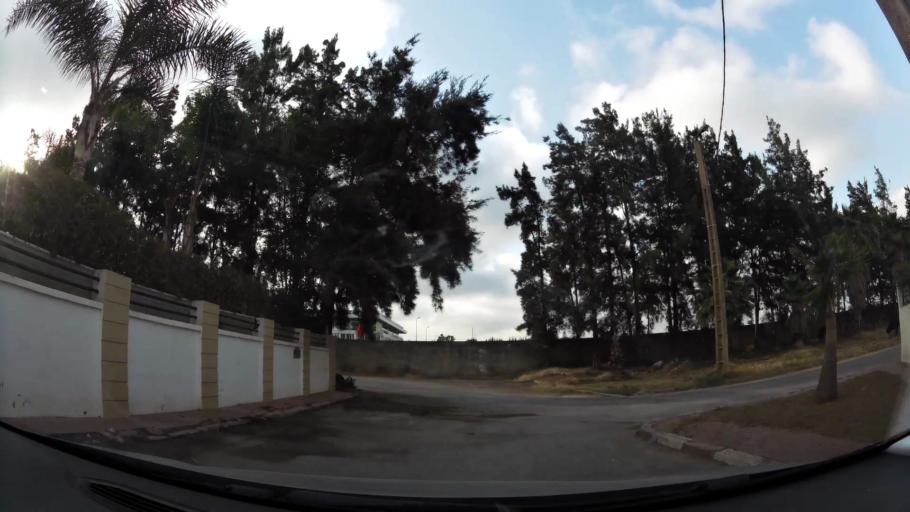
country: MA
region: Rabat-Sale-Zemmour-Zaer
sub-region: Rabat
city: Rabat
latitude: 33.9539
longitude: -6.8448
